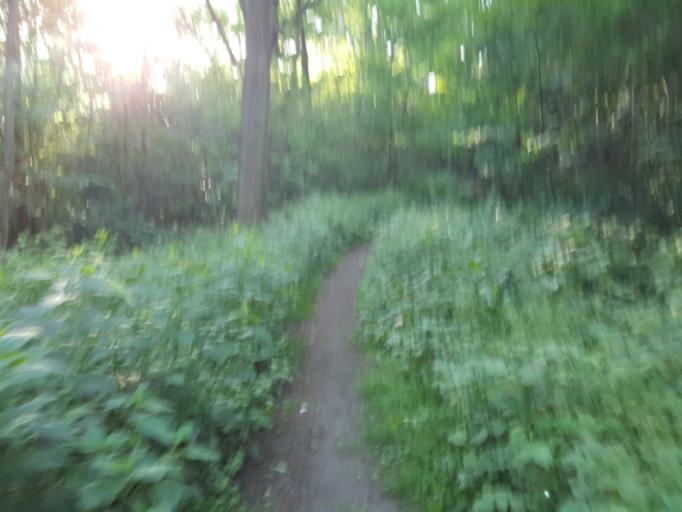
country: DE
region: Schleswig-Holstein
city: Oststeinbek
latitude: 53.5088
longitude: 10.1675
